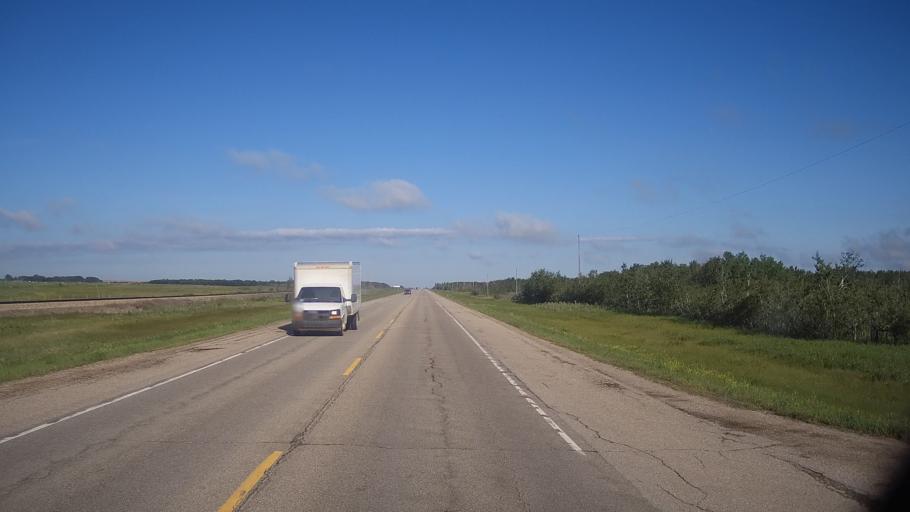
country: CA
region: Saskatchewan
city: Lanigan
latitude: 51.8532
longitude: -105.0762
